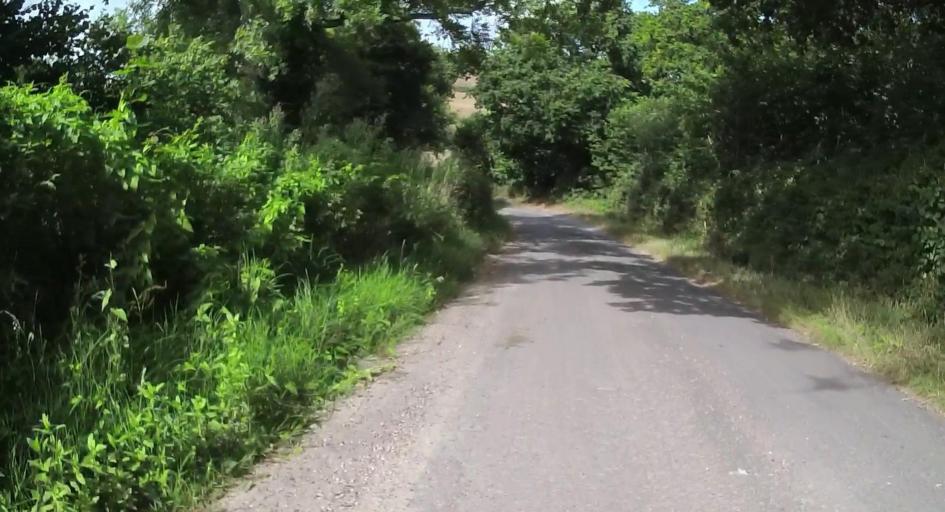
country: GB
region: England
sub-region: Dorset
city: Swanage
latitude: 50.6204
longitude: -1.9865
